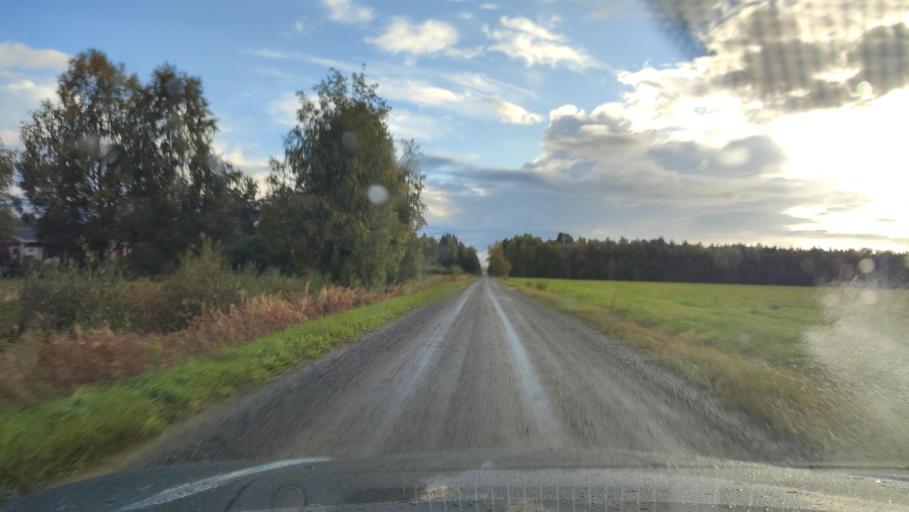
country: FI
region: Southern Ostrobothnia
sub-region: Suupohja
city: Karijoki
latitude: 62.3226
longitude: 21.5692
